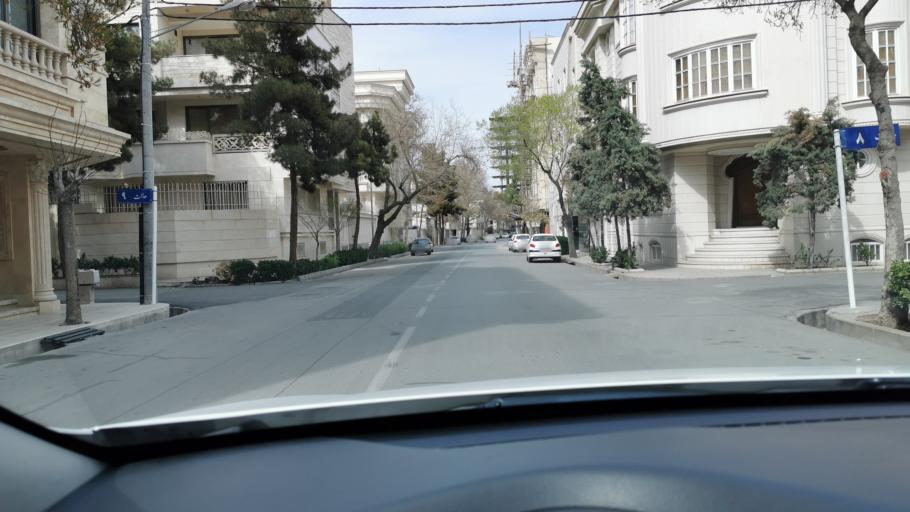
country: IR
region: Razavi Khorasan
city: Mashhad
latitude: 36.2925
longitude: 59.5747
